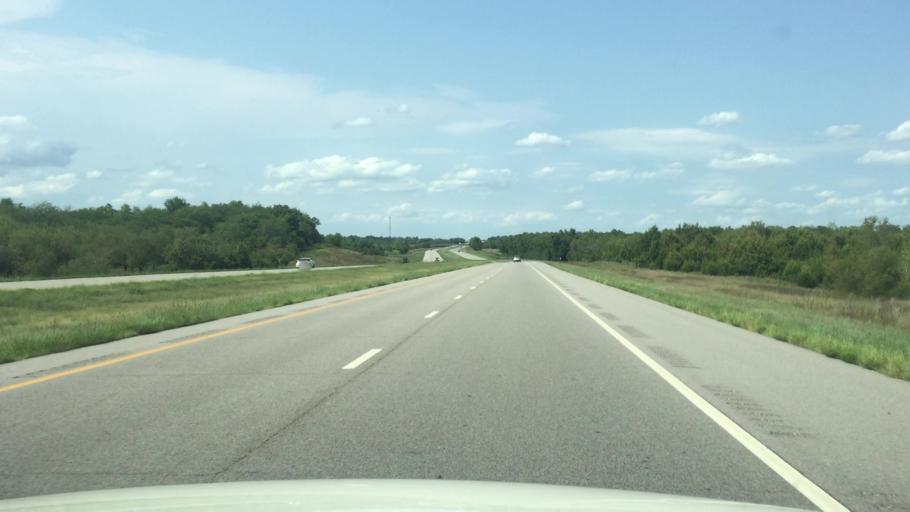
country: US
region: Kansas
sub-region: Linn County
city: La Cygne
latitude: 38.4473
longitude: -94.6859
